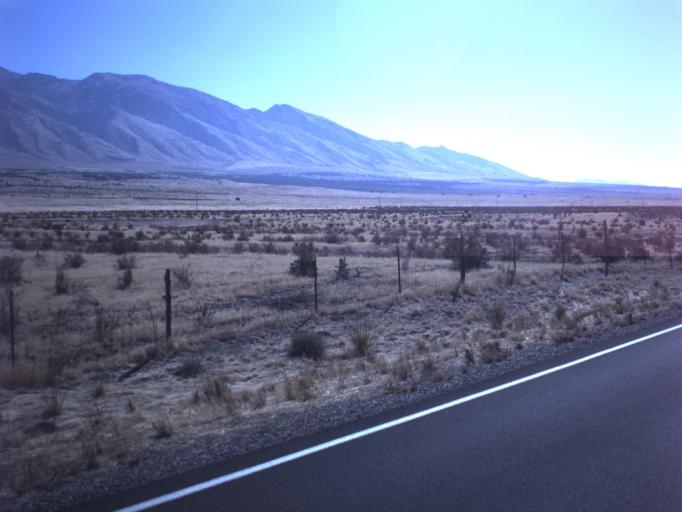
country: US
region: Utah
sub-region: Tooele County
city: Grantsville
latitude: 40.4863
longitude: -112.7461
